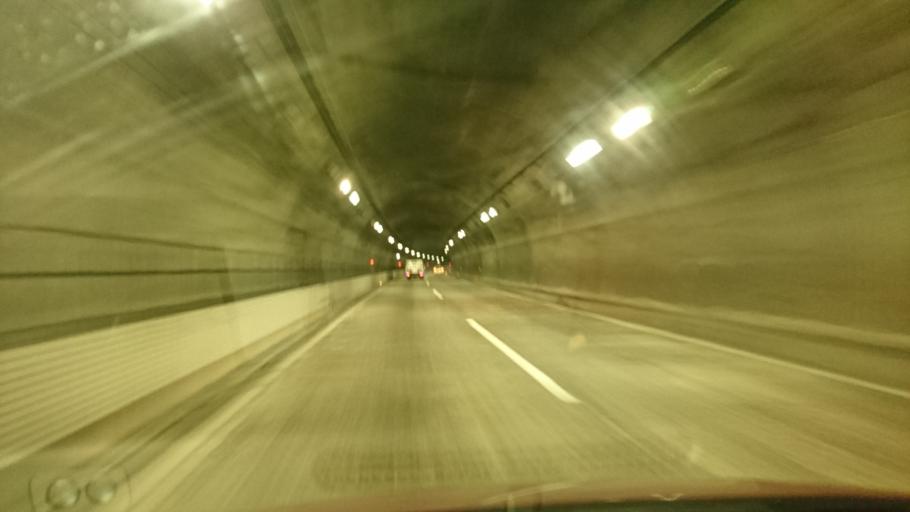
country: JP
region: Okayama
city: Okayama-shi
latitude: 34.7723
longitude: 134.1067
